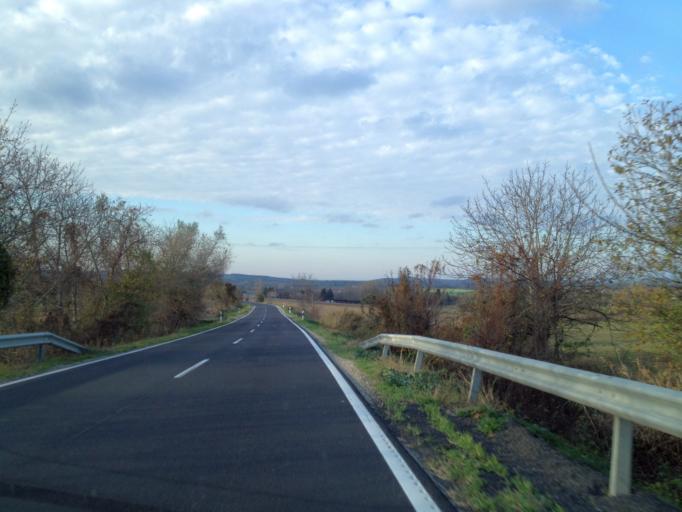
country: HU
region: Gyor-Moson-Sopron
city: Bakonyszentlaszlo
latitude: 47.4251
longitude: 17.8402
